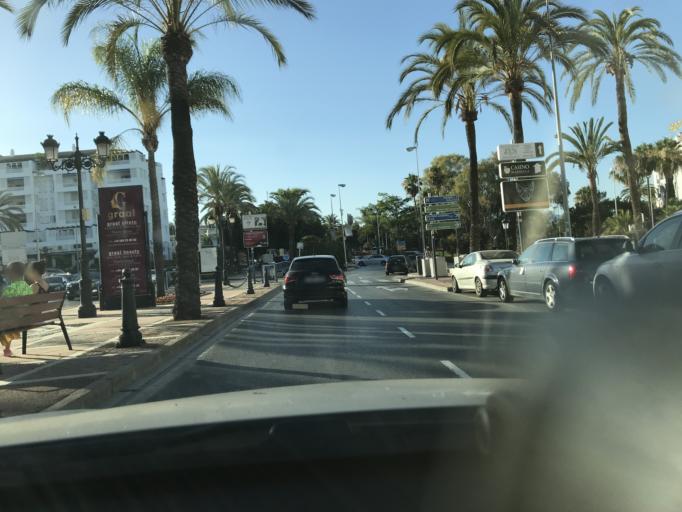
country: ES
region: Andalusia
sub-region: Provincia de Malaga
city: Marbella
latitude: 36.4877
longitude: -4.9562
